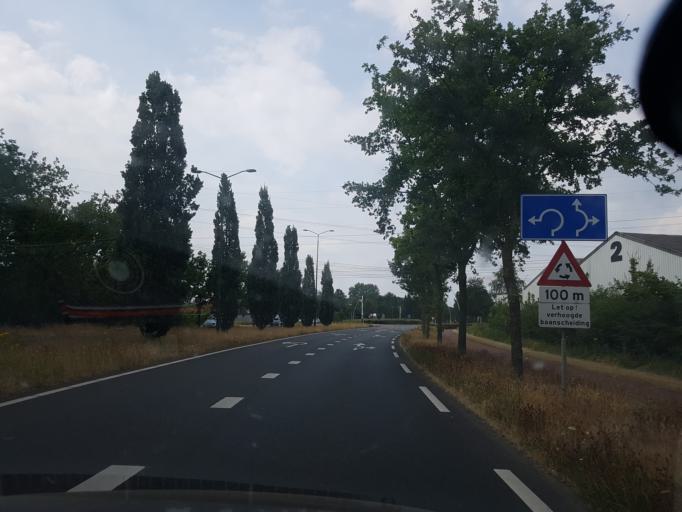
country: NL
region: North Brabant
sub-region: Gemeente Nuenen, Gerwen en Nederwetten
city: Nuenen
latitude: 51.4476
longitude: 5.5522
